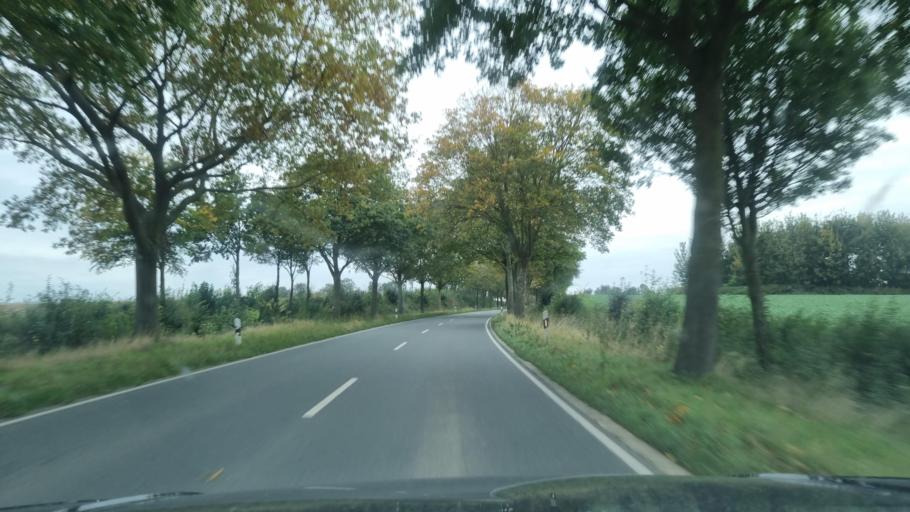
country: DE
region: North Rhine-Westphalia
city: Kalkar
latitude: 51.7096
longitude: 6.3130
